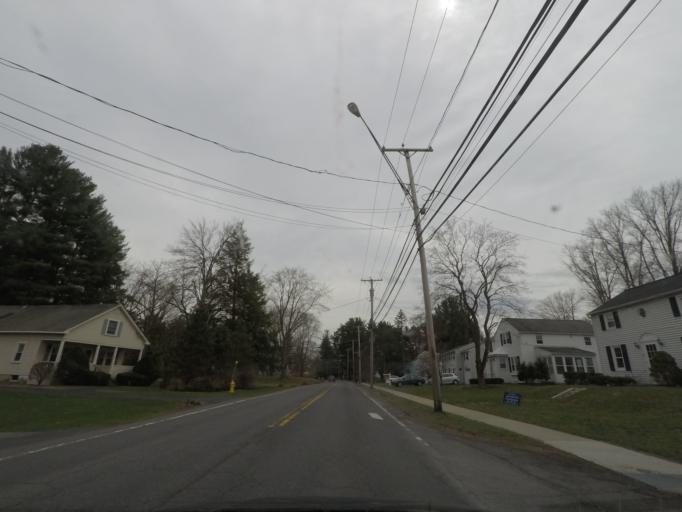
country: US
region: New York
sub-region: Albany County
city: Delmar
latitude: 42.6130
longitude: -73.8206
